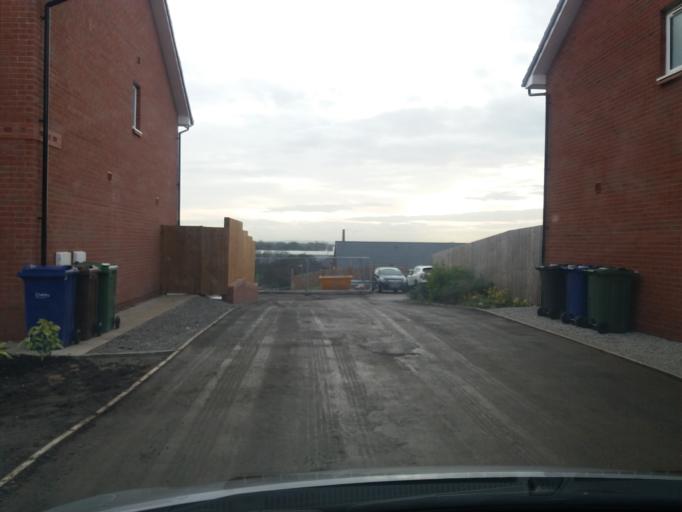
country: GB
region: England
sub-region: Lancashire
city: Adlington
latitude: 53.6137
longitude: -2.5947
